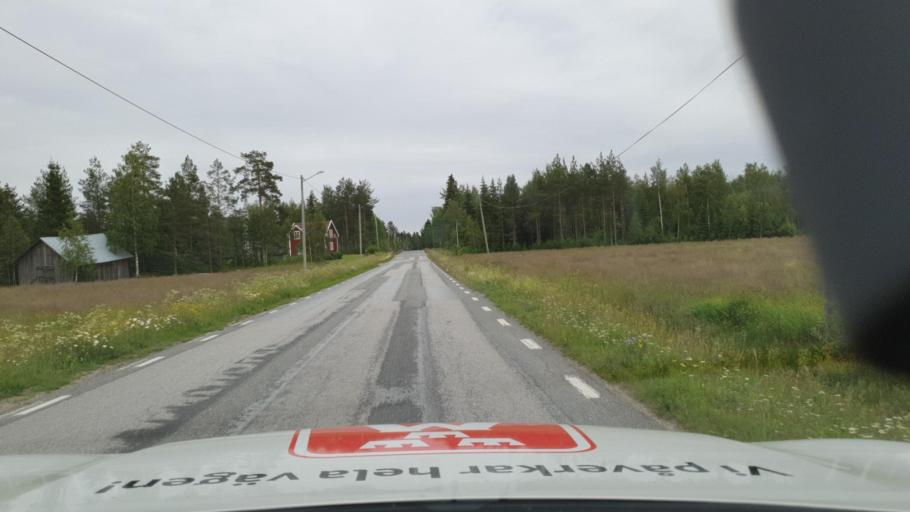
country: SE
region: Vaesterbotten
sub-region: Nordmalings Kommun
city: Nordmaling
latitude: 63.5308
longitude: 19.4059
